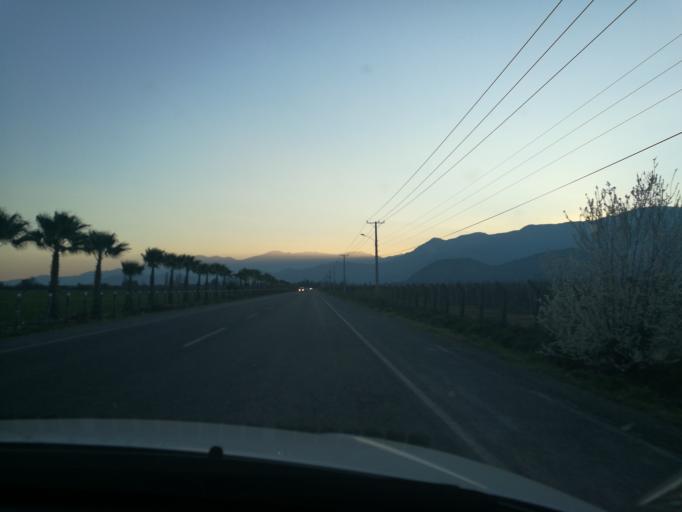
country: CL
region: O'Higgins
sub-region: Provincia de Cachapoal
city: Graneros
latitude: -34.0361
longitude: -70.6804
